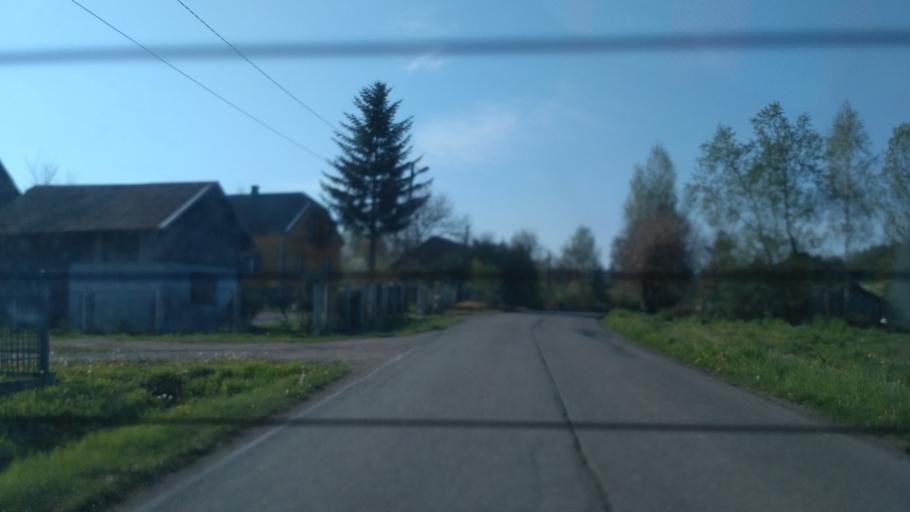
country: PL
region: Subcarpathian Voivodeship
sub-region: Powiat jaroslawski
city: Pruchnik
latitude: 49.8778
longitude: 22.5643
